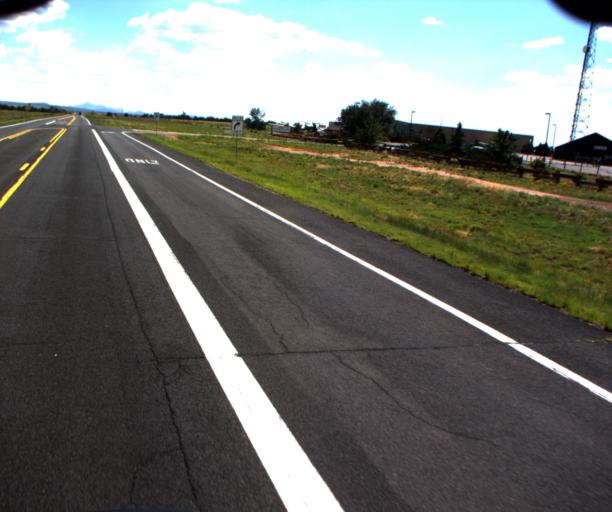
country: US
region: Arizona
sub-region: Coconino County
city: Grand Canyon Village
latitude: 35.6495
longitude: -112.1399
